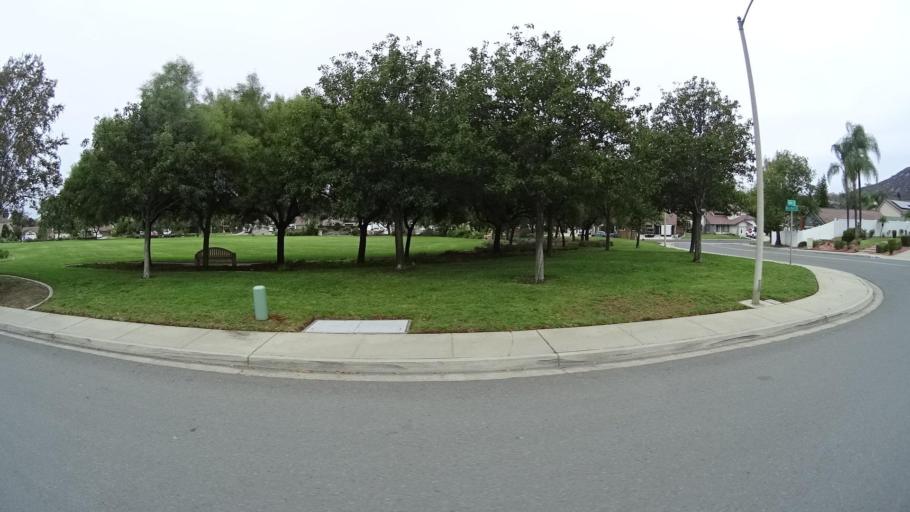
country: US
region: California
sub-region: San Diego County
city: Rancho San Diego
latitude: 32.7583
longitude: -116.9104
